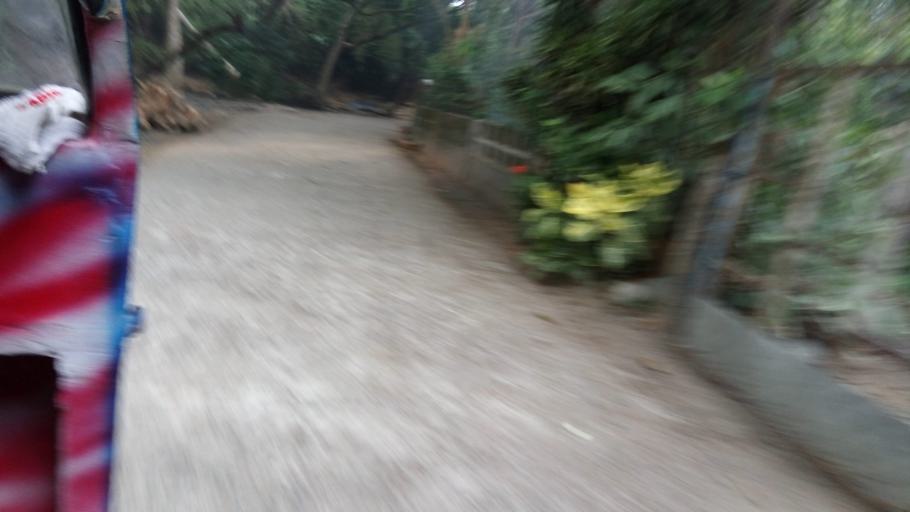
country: PH
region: Ilocos
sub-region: Province of La Union
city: Santo Tomas
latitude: 16.2881
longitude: 120.3805
